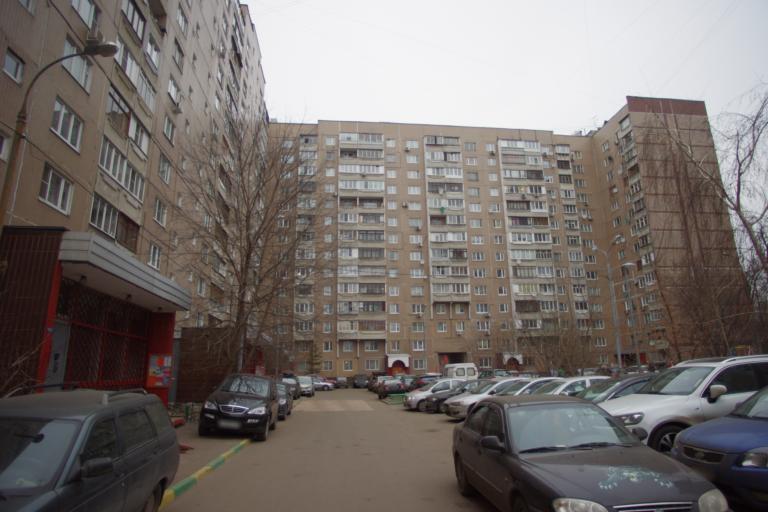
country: RU
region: Moscow
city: Lefortovo
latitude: 55.7725
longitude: 37.7302
